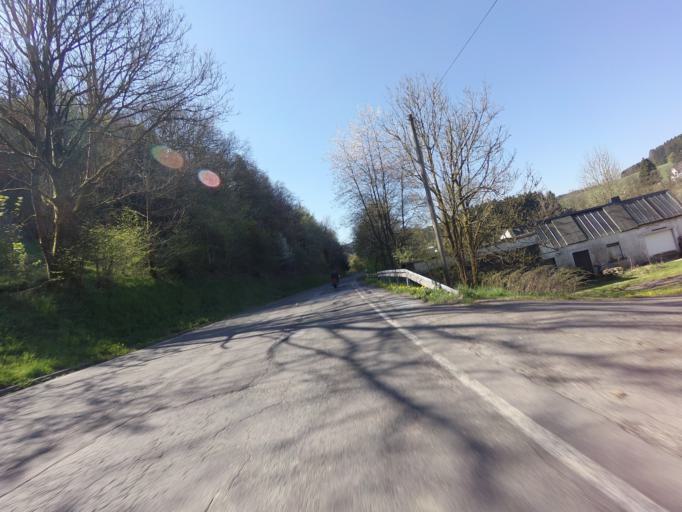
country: DE
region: North Rhine-Westphalia
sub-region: Regierungsbezirk Arnsberg
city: Drolshagen
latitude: 51.0829
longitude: 7.7586
